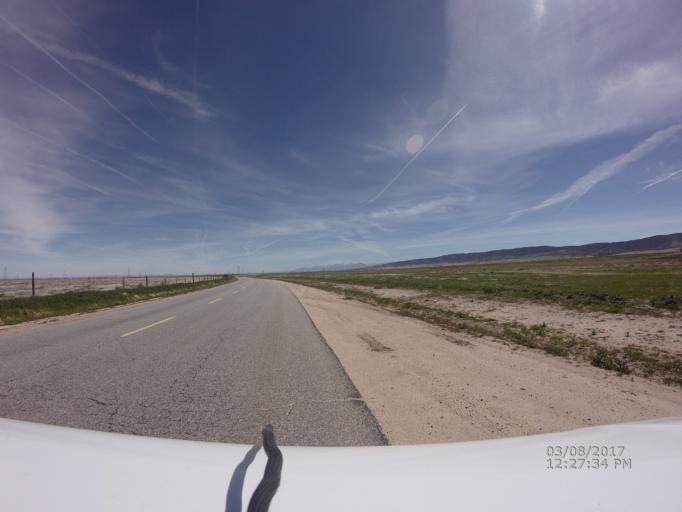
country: US
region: California
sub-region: Los Angeles County
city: Green Valley
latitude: 34.7125
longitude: -118.3491
